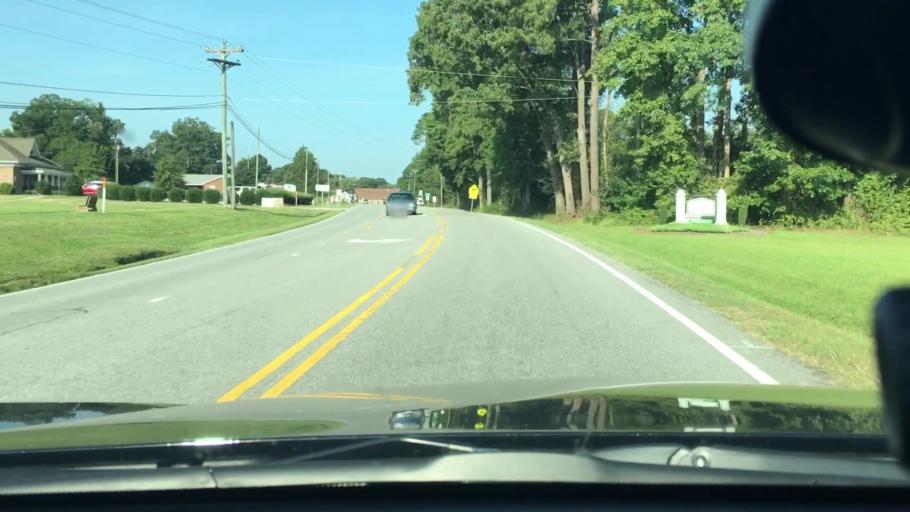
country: US
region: North Carolina
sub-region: Edgecombe County
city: Pinetops
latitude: 35.7891
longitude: -77.6271
